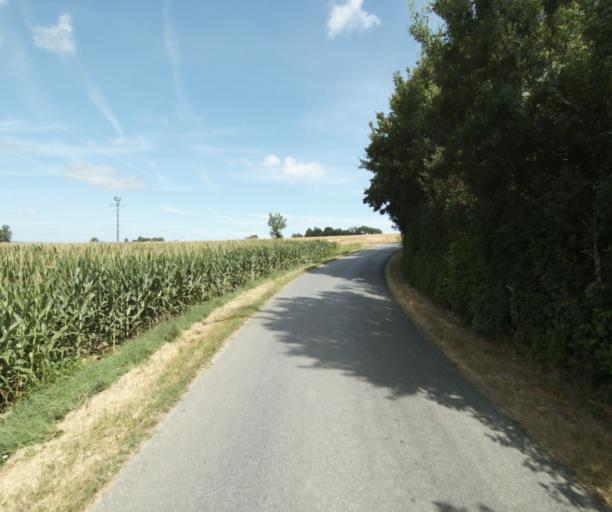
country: FR
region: Midi-Pyrenees
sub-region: Departement du Tarn
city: Dourgne
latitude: 43.5048
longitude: 2.0903
